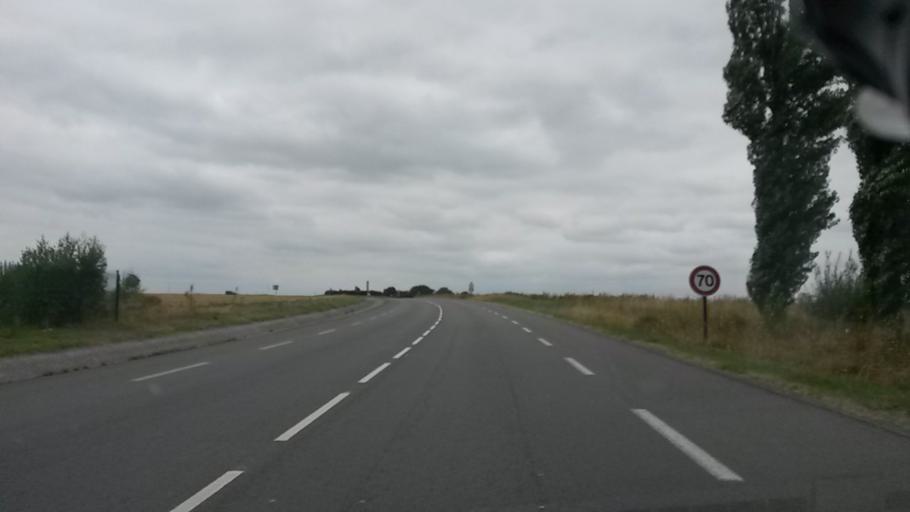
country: FR
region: Nord-Pas-de-Calais
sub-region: Departement du Pas-de-Calais
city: Bapaume
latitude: 50.1151
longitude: 2.8497
